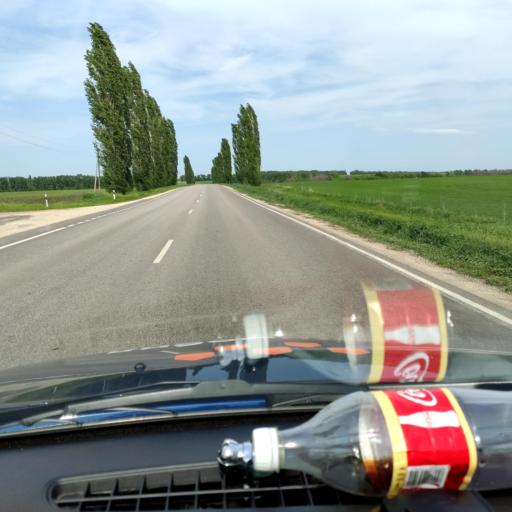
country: RU
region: Voronezj
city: Novaya Usman'
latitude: 51.5474
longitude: 39.3629
